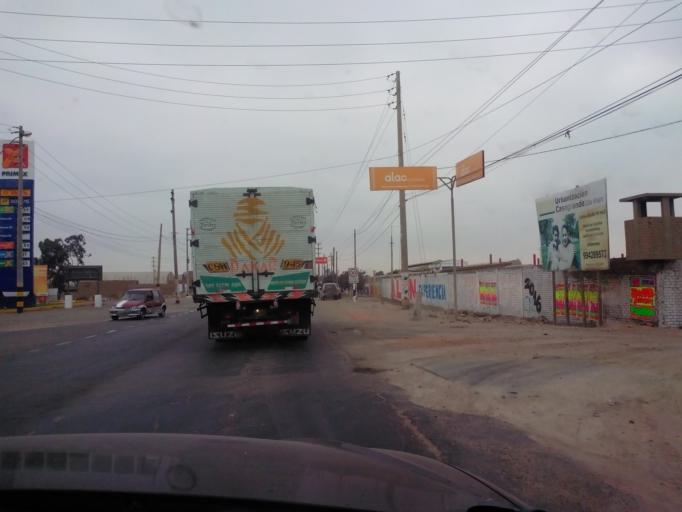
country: PE
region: Ica
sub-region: Provincia de Chincha
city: Chincha Baja
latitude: -13.4511
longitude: -76.1362
